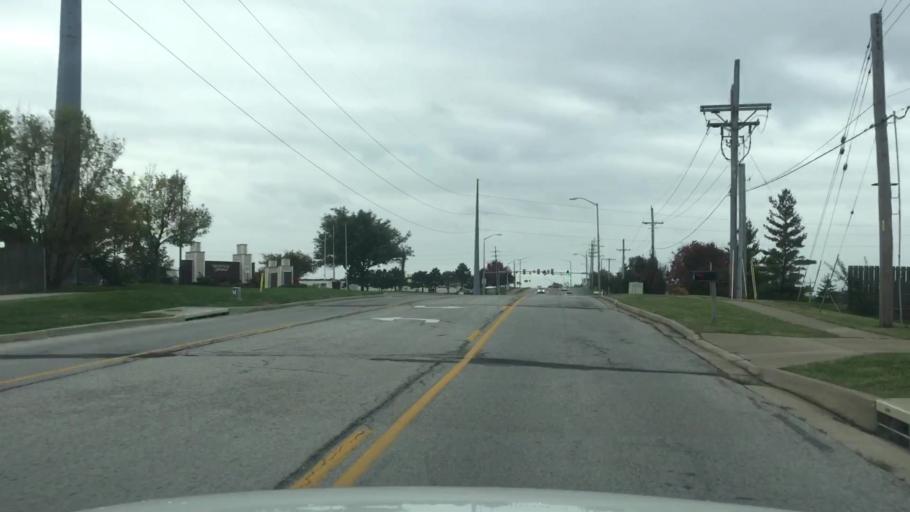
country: US
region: Kansas
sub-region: Johnson County
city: Shawnee
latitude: 39.0132
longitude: -94.7707
